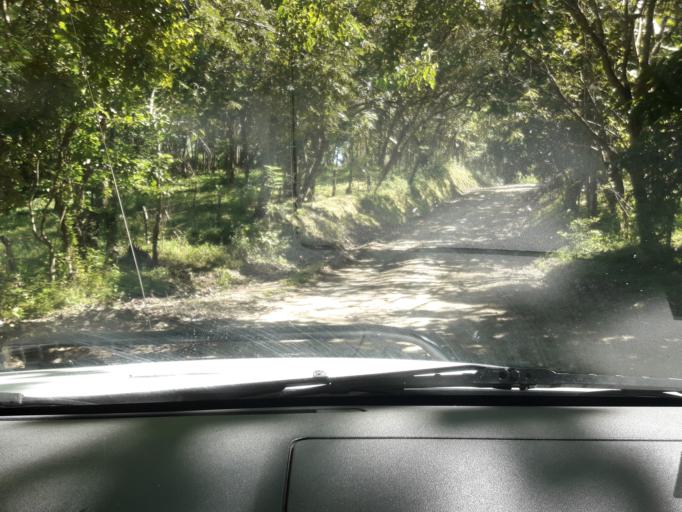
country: NI
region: Rivas
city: Cardenas
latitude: 11.2307
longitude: -85.6484
